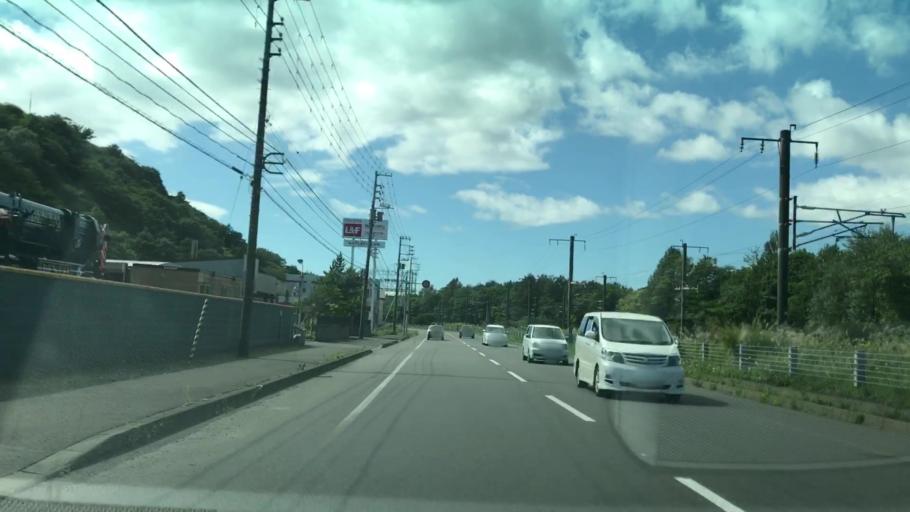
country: JP
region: Hokkaido
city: Muroran
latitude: 42.3346
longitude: 140.9982
